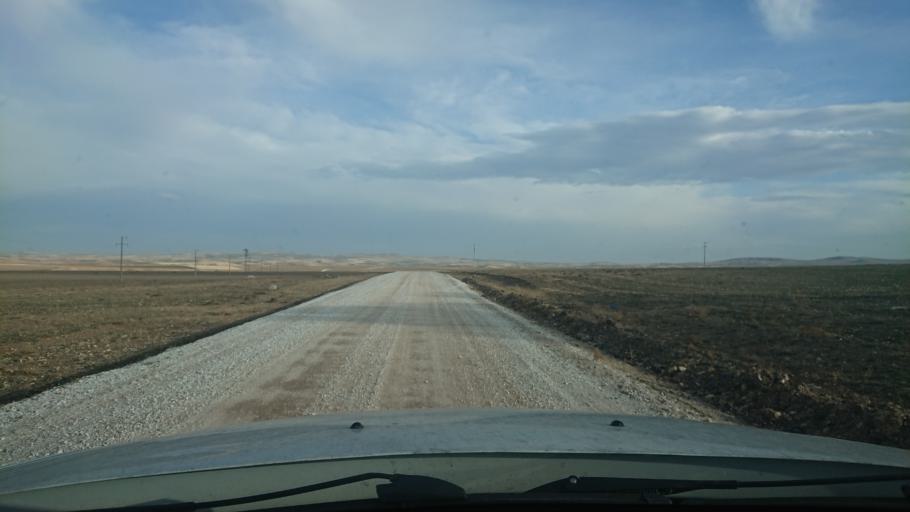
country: TR
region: Aksaray
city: Agacoren
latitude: 38.7220
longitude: 33.8667
